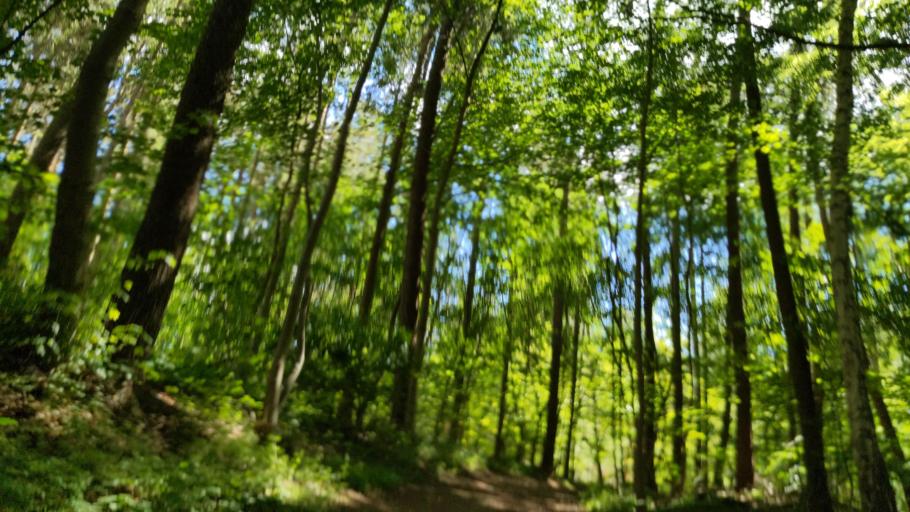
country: DE
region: Schleswig-Holstein
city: Einhaus
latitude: 53.7233
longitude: 10.7414
